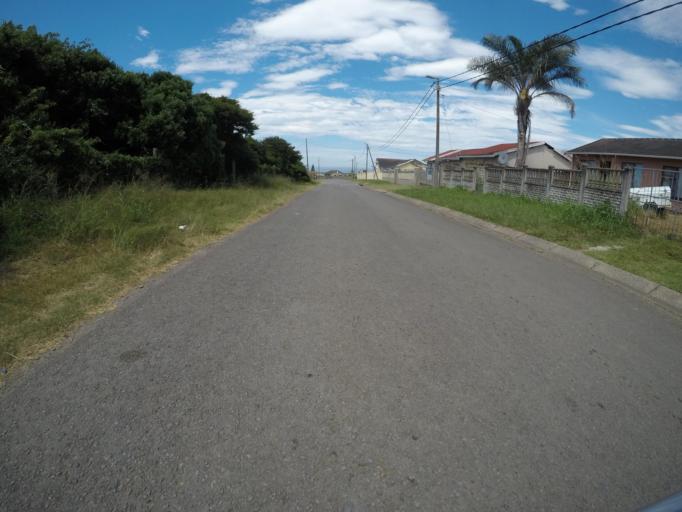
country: ZA
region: Eastern Cape
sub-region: Buffalo City Metropolitan Municipality
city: East London
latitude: -33.0419
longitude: 27.8672
